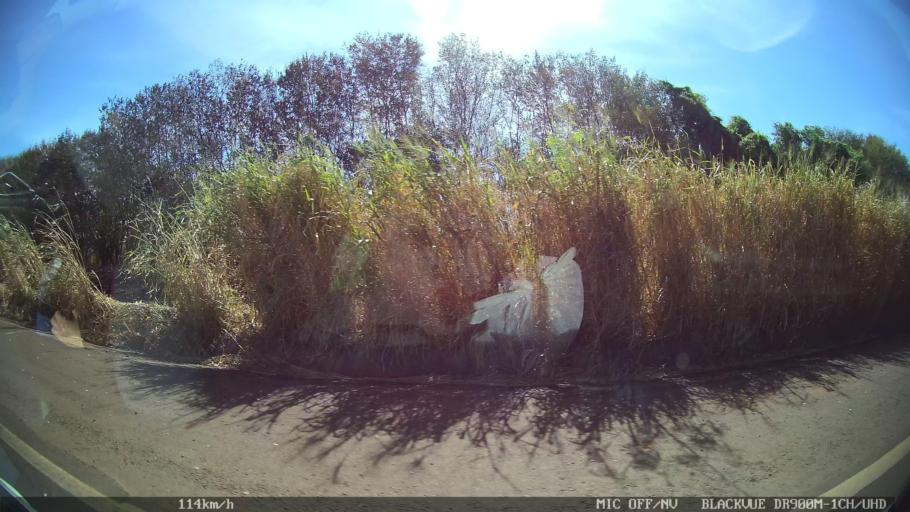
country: BR
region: Sao Paulo
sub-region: Franca
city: Franca
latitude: -20.5577
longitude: -47.5961
